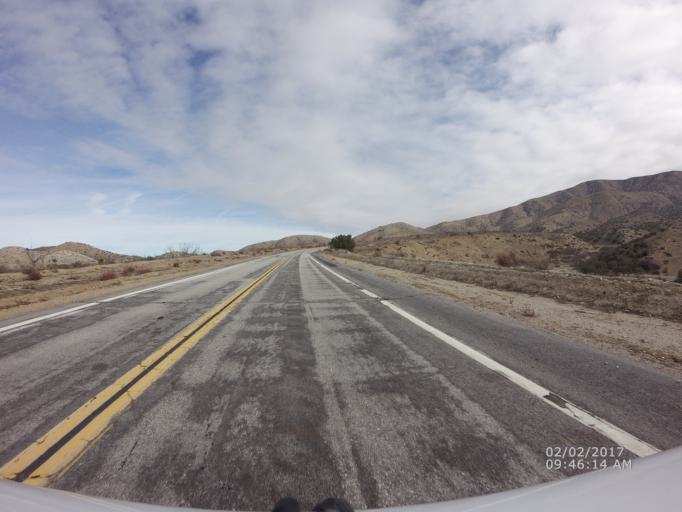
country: US
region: California
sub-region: Los Angeles County
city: Vincent
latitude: 34.4573
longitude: -118.0904
